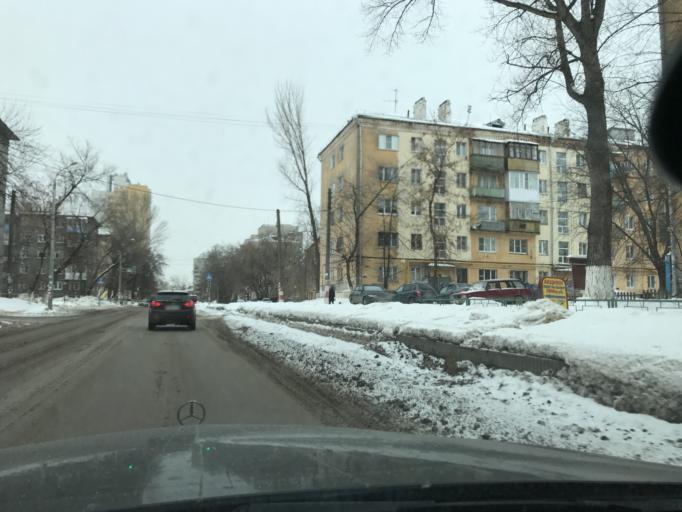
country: RU
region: Nizjnij Novgorod
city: Nizhniy Novgorod
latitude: 56.3303
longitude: 43.9588
